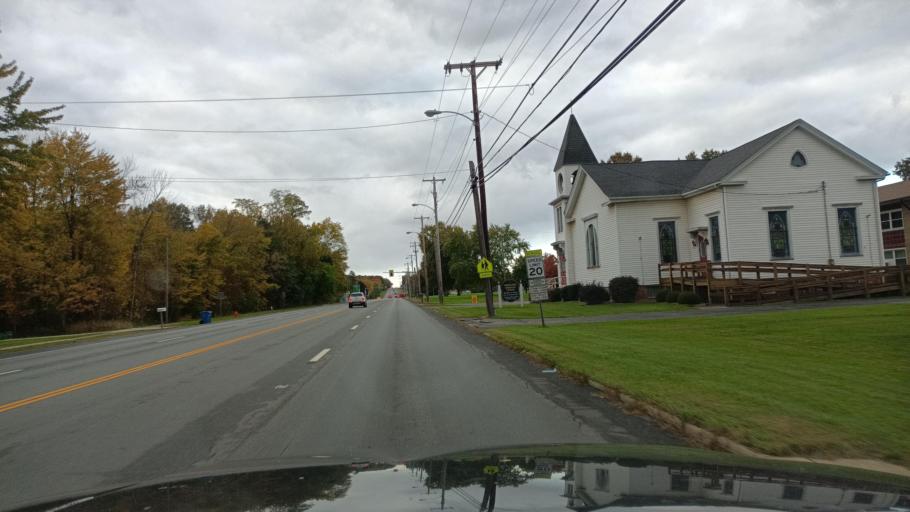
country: US
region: Ohio
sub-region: Trumbull County
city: Lordstown
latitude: 41.1693
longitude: -80.8574
